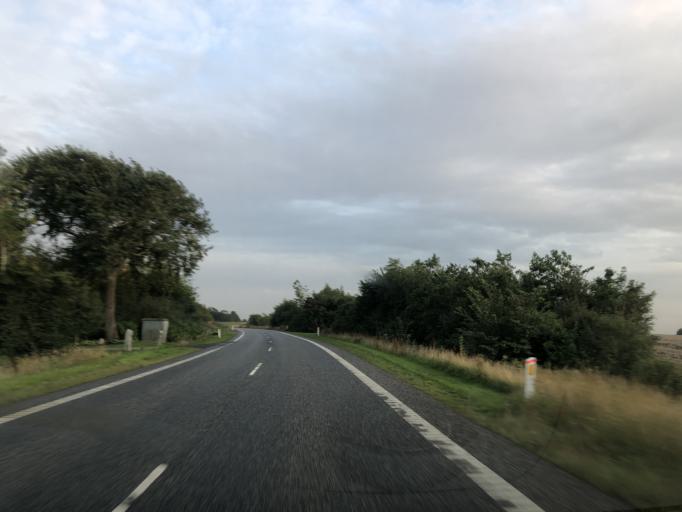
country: DK
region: Central Jutland
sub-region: Holstebro Kommune
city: Vinderup
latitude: 56.6024
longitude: 8.8778
